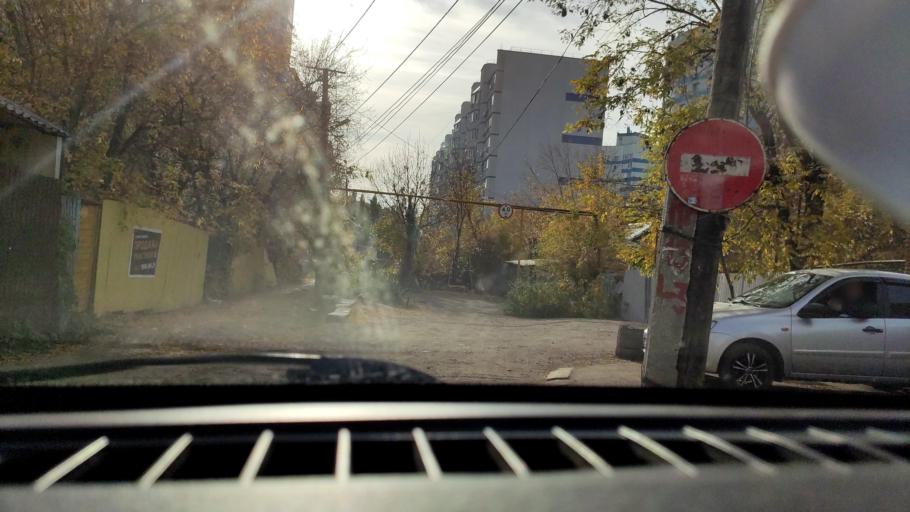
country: RU
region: Samara
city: Samara
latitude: 53.2253
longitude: 50.1765
